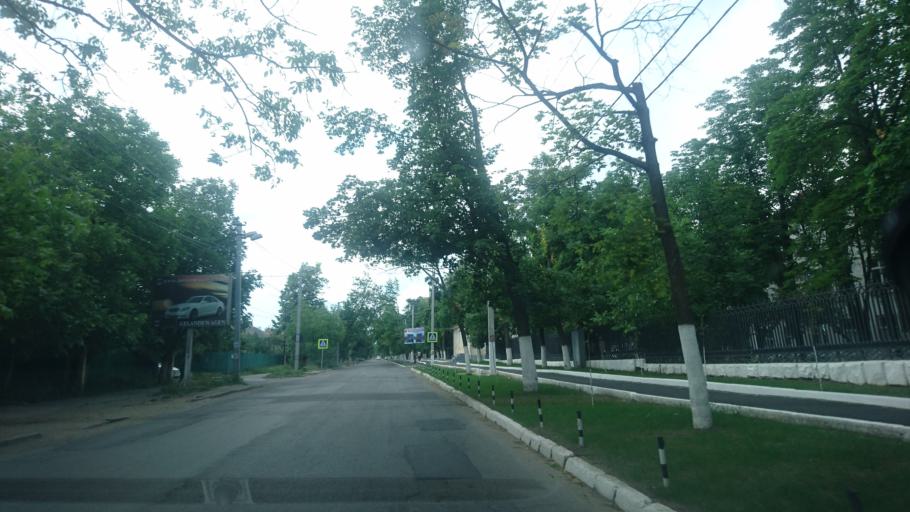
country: MD
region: Chisinau
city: Stauceni
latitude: 47.0564
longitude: 28.8401
